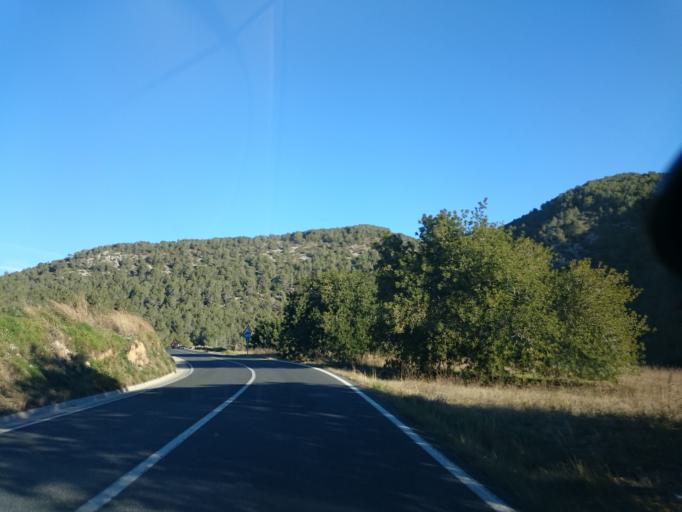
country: ES
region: Catalonia
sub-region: Provincia de Barcelona
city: Sant Pere de Ribes
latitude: 41.2712
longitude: 1.7676
